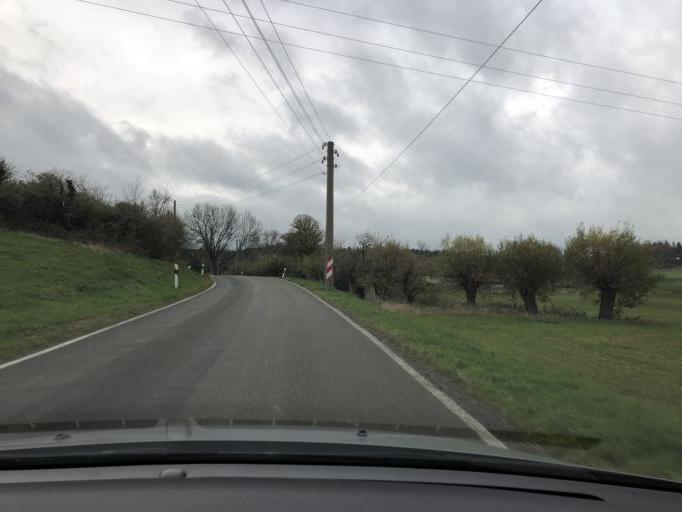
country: DE
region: Thuringia
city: Dreitzsch
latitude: 50.7290
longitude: 11.8159
